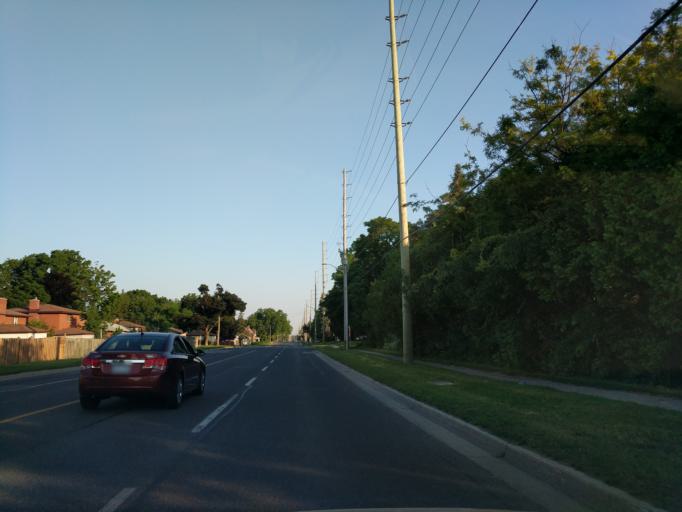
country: CA
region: Ontario
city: Oshawa
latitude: 43.9010
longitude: -78.8976
